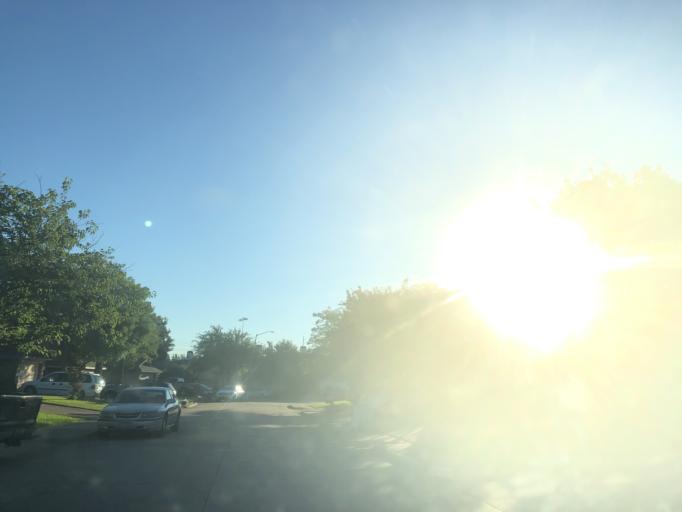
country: US
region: Texas
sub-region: Dallas County
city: Garland
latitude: 32.8379
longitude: -96.6368
